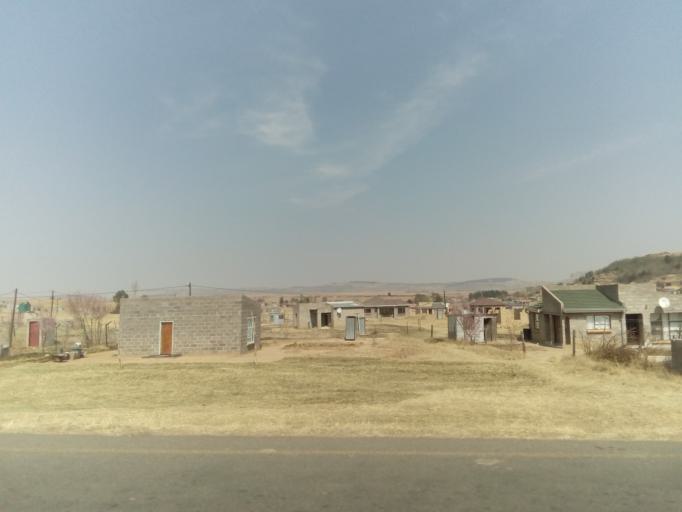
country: LS
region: Leribe
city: Maputsoe
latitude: -28.9377
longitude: 27.9446
